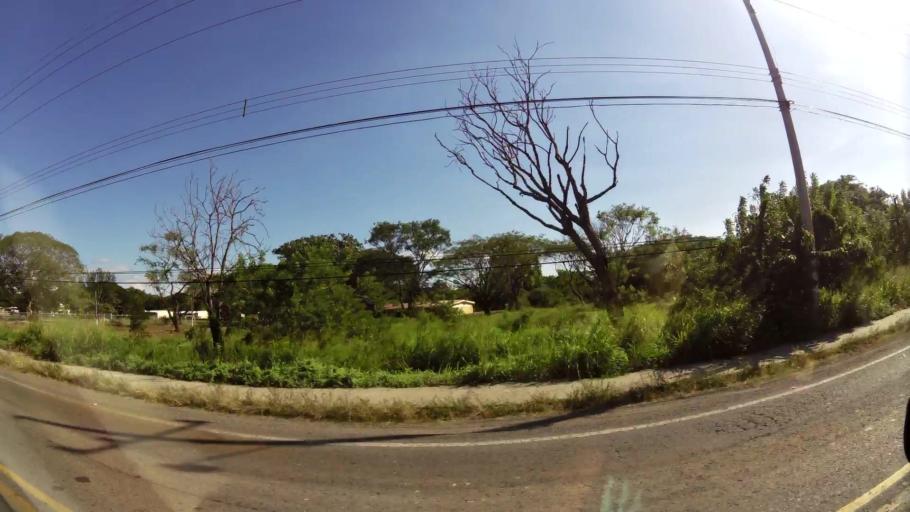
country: CR
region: Guanacaste
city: Liberia
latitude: 10.6210
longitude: -85.4556
